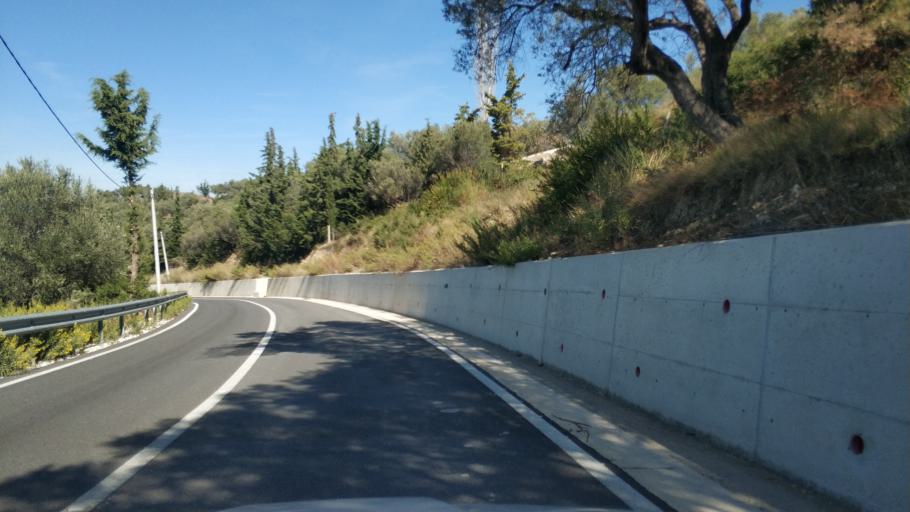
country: AL
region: Vlore
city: Vlore
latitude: 40.4539
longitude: 19.5153
